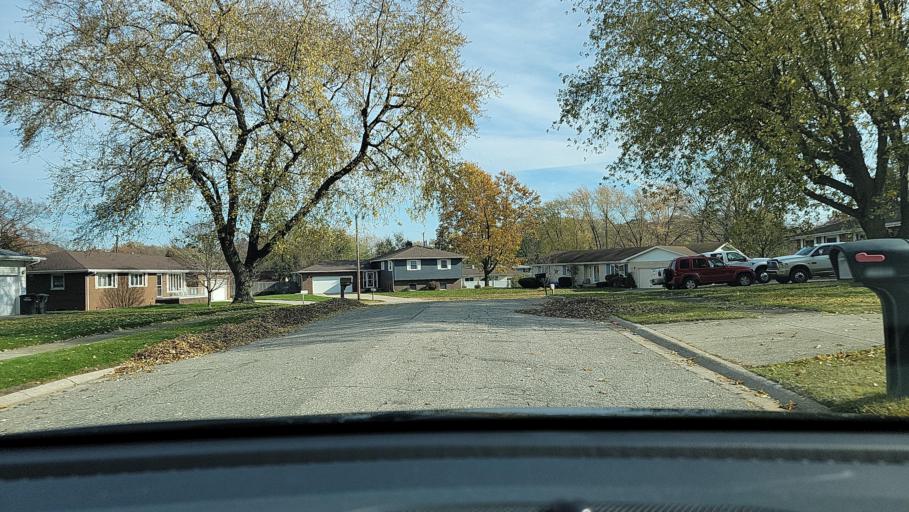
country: US
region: Indiana
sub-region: Porter County
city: Portage
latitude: 41.5782
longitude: -87.2061
